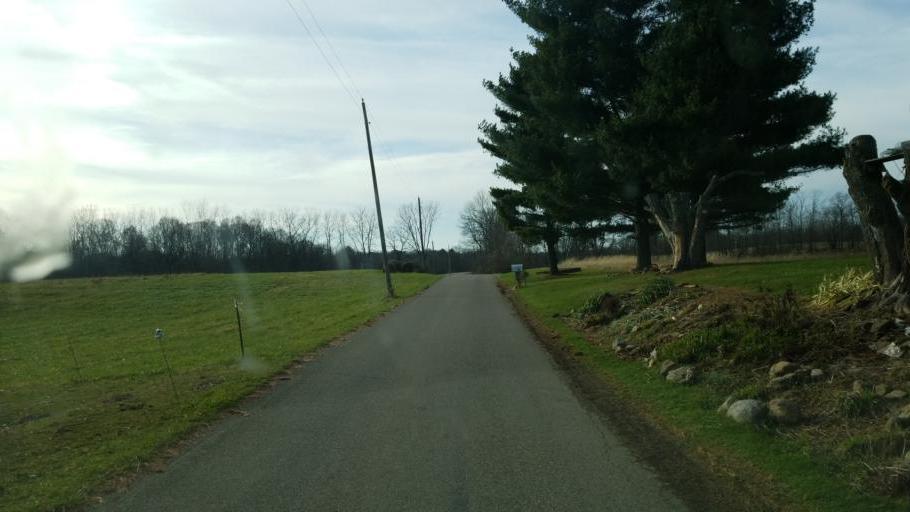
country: US
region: Ohio
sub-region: Knox County
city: Fredericktown
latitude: 40.4858
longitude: -82.6331
